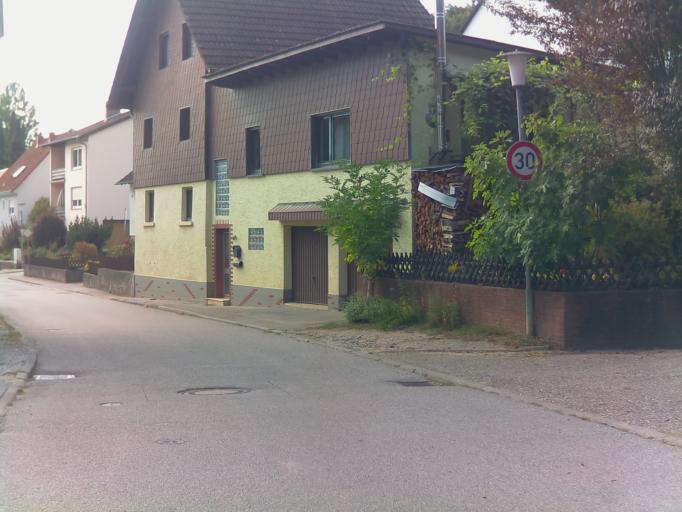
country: DE
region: Baden-Wuerttemberg
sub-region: Karlsruhe Region
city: Laudenbach
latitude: 49.6156
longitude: 8.6810
